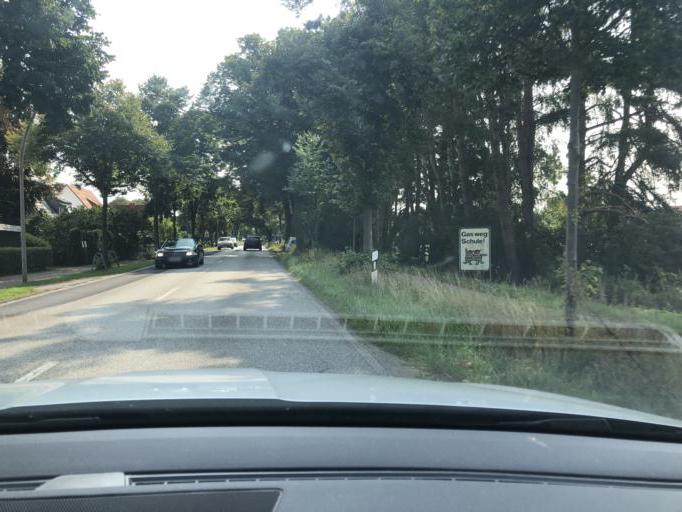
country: DE
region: Schleswig-Holstein
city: Gross Gronau
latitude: 53.8126
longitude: 10.7423
